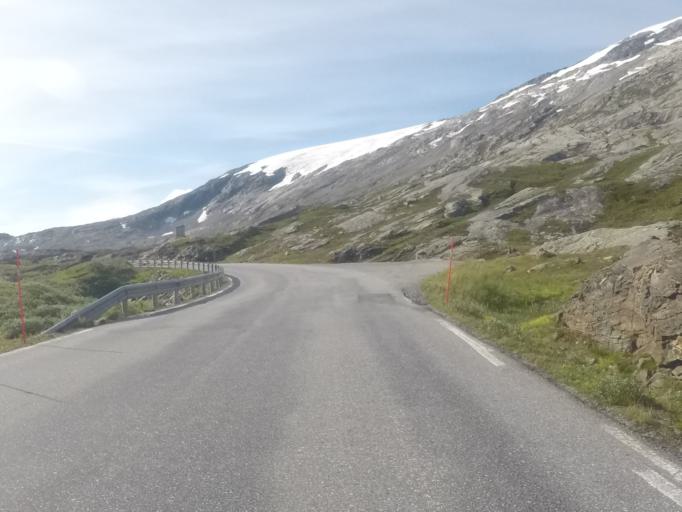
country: NO
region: More og Romsdal
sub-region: Norddal
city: Valldal
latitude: 62.0388
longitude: 7.2578
